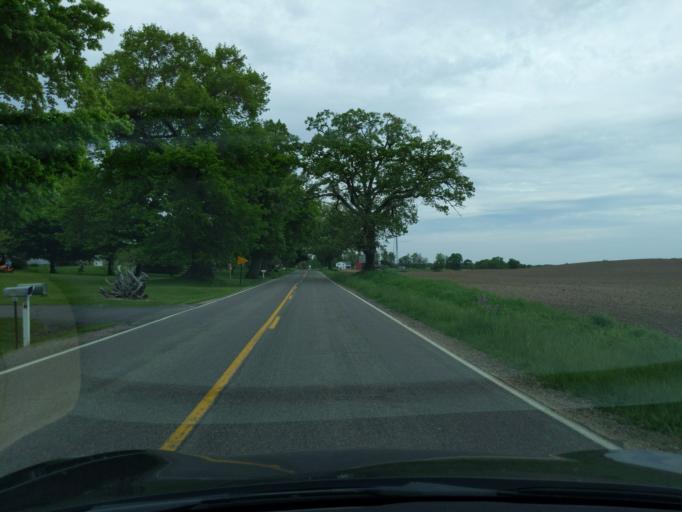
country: US
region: Michigan
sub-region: Ingham County
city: Mason
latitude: 42.5437
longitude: -84.3567
